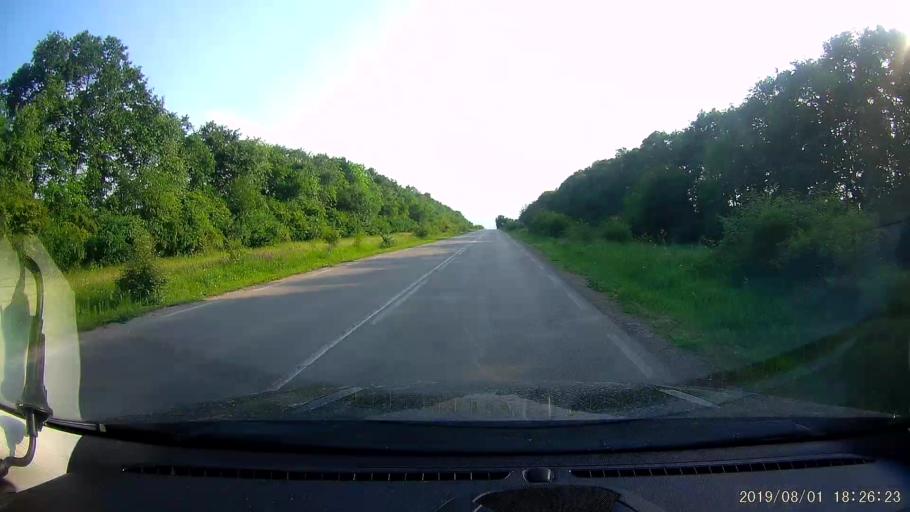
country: BG
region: Shumen
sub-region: Obshtina Venets
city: Venets
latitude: 43.6017
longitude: 26.9933
